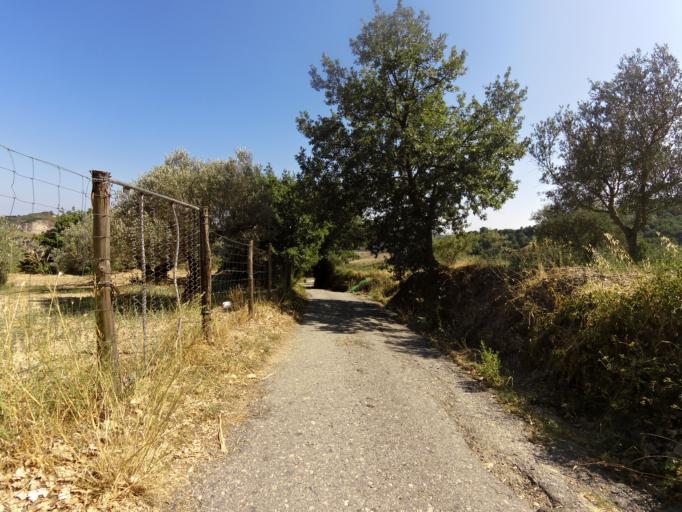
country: IT
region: Calabria
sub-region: Provincia di Reggio Calabria
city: Pazzano
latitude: 38.4590
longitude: 16.4584
